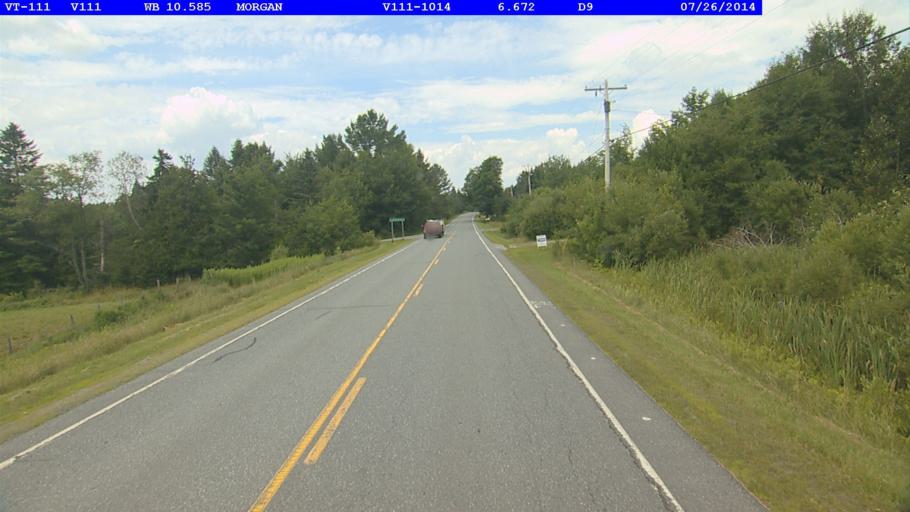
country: US
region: Vermont
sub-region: Orleans County
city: Newport
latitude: 44.8875
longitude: -71.9631
